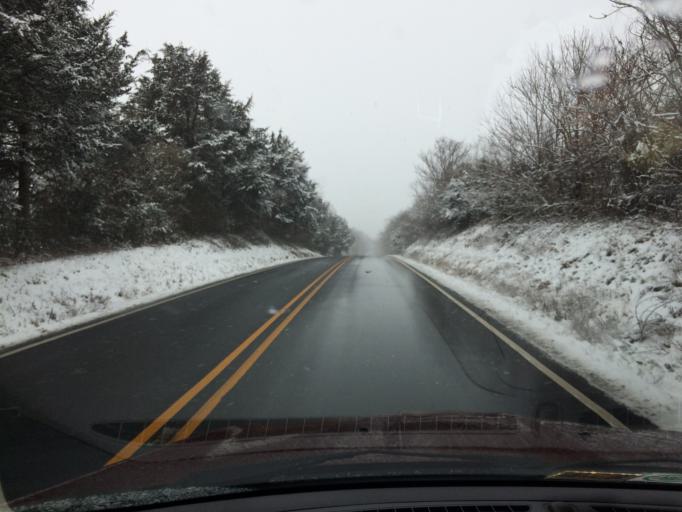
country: US
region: Virginia
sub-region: Amherst County
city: Amherst
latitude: 37.5975
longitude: -79.0577
